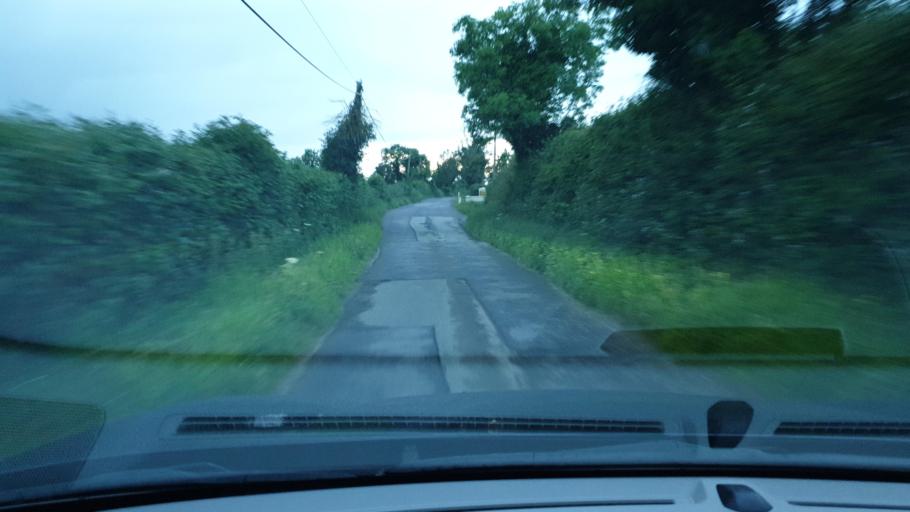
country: IE
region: Leinster
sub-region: An Mhi
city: Ashbourne
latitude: 53.5118
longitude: -6.3557
